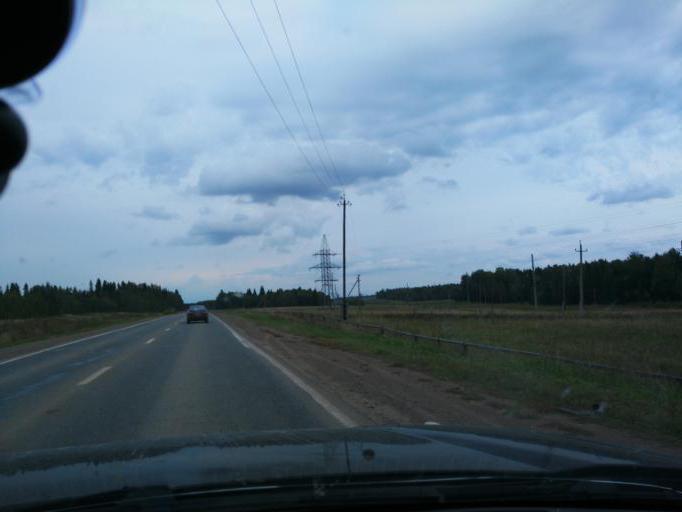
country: RU
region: Perm
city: Chernushka
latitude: 56.5304
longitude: 56.0447
